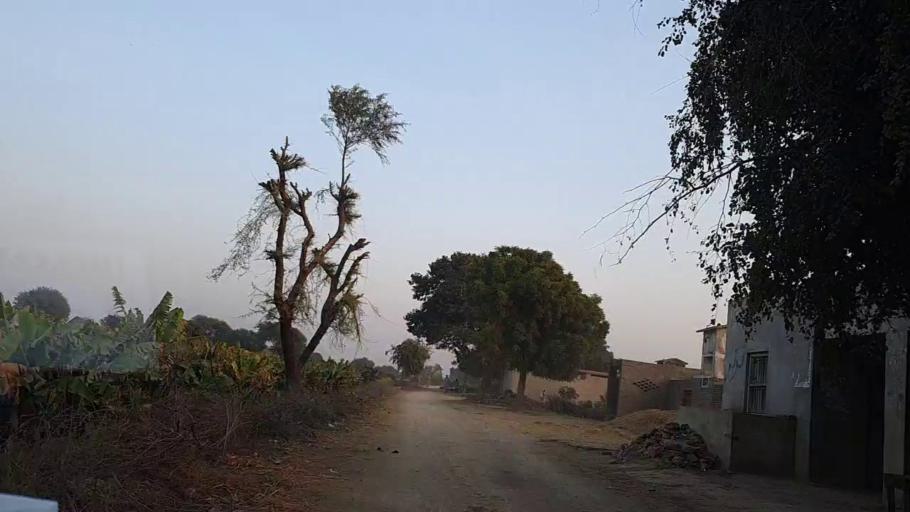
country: PK
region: Sindh
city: Tando Ghulam Ali
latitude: 25.1743
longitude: 68.9264
